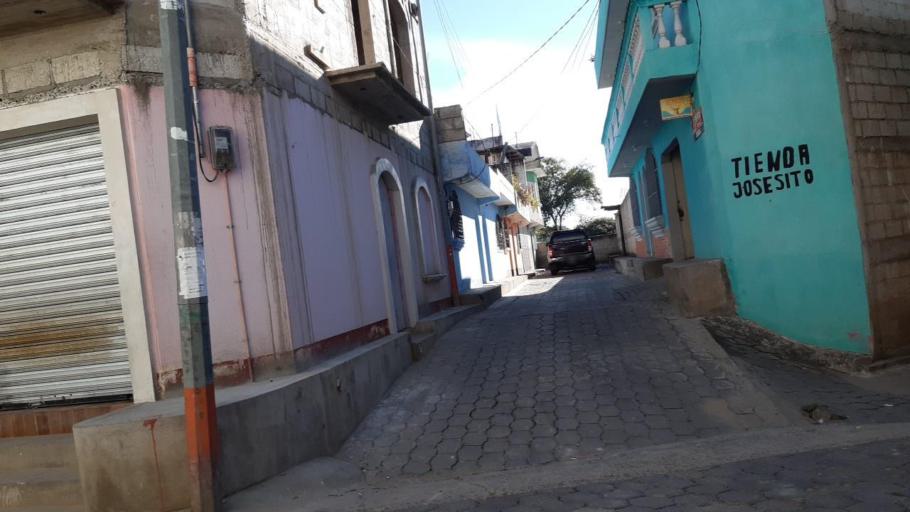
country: GT
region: Quetzaltenango
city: Salcaja
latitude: 14.8778
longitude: -91.4533
